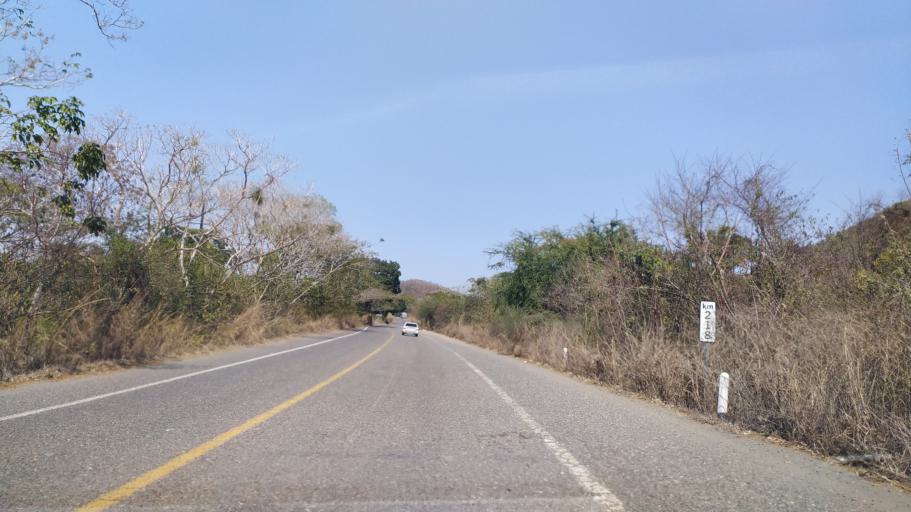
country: MX
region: Michoacan
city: Coahuayana Viejo
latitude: 18.6369
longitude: -103.6673
